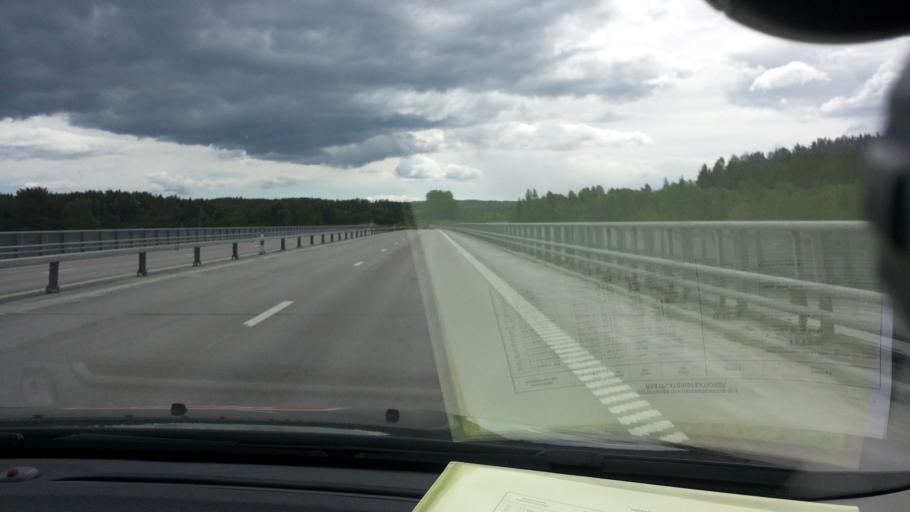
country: SE
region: Vaesternorrland
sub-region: Sundsvalls Kommun
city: Nolby
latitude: 62.2756
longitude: 17.3448
